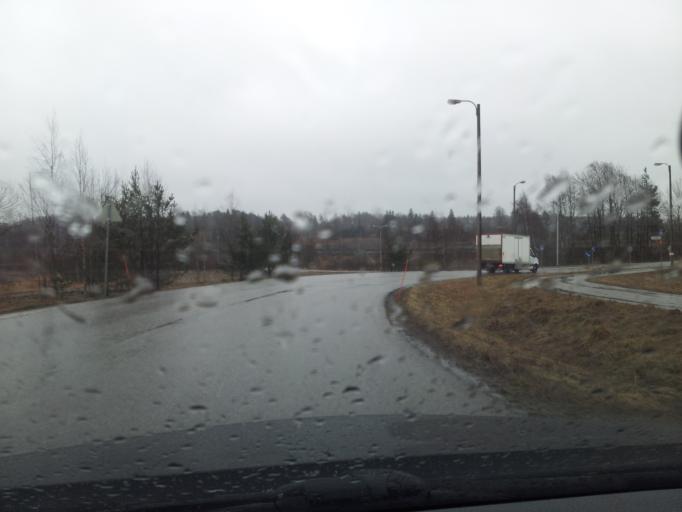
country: FI
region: Uusimaa
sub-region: Helsinki
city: Kirkkonummi
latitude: 60.1371
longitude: 24.5134
